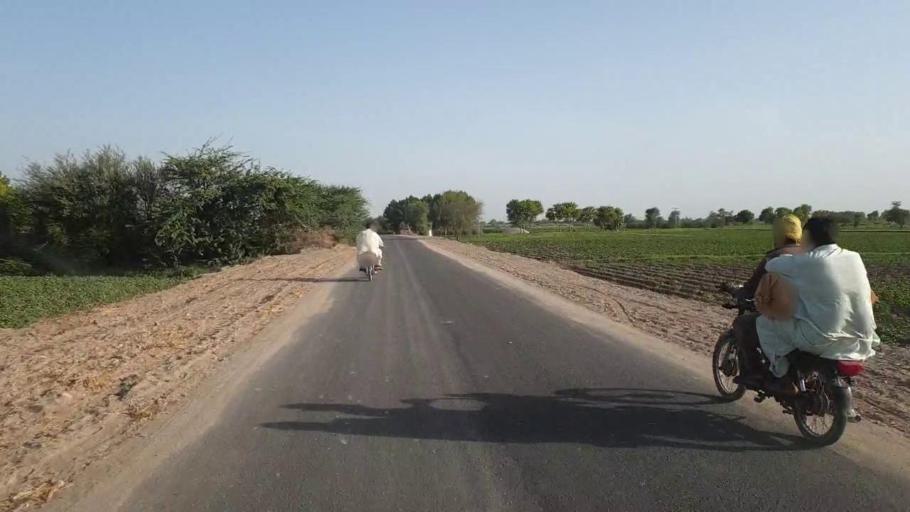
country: PK
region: Sindh
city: Jam Sahib
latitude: 26.3428
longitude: 68.5689
